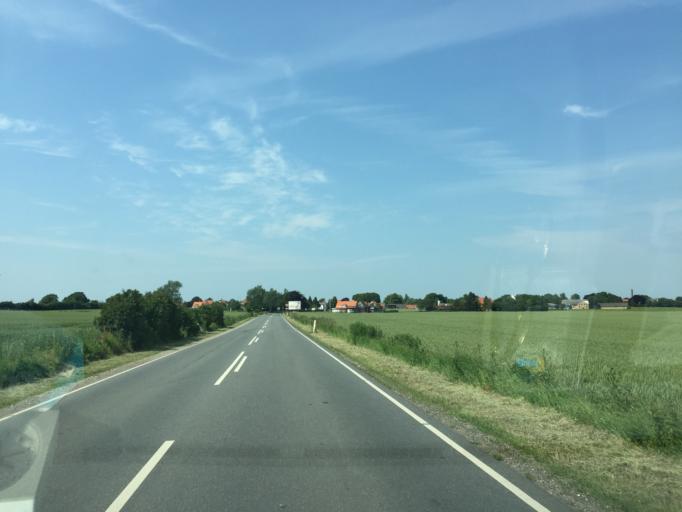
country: DK
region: South Denmark
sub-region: Kerteminde Kommune
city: Kerteminde
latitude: 55.4944
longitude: 10.6532
